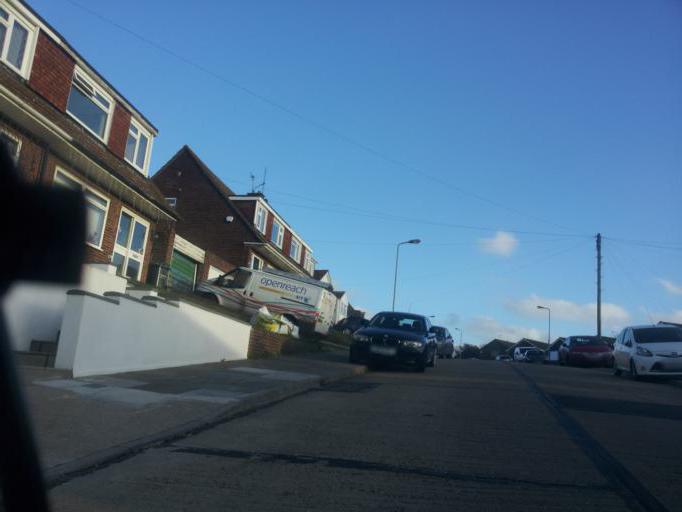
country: GB
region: England
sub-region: Kent
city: Meopham
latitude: 51.4070
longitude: 0.3434
